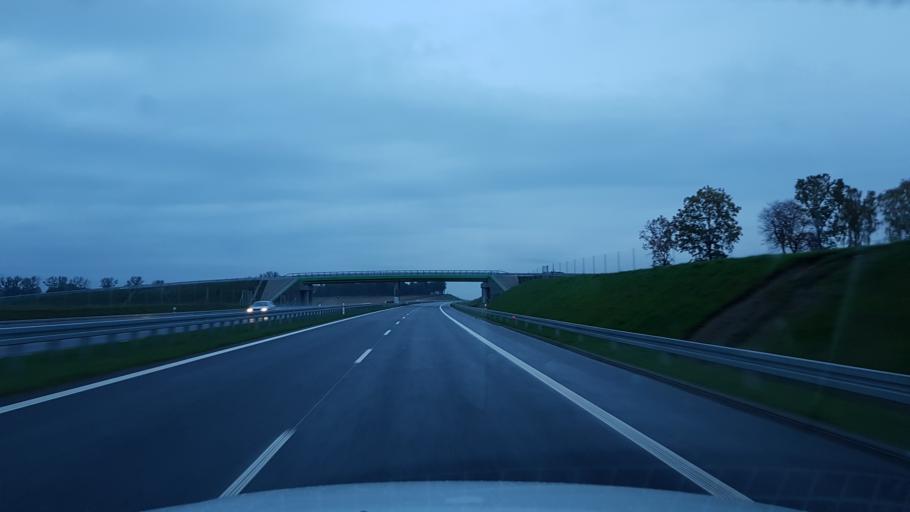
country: PL
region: West Pomeranian Voivodeship
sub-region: Powiat gryficki
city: Brojce
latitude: 53.9062
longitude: 15.3813
